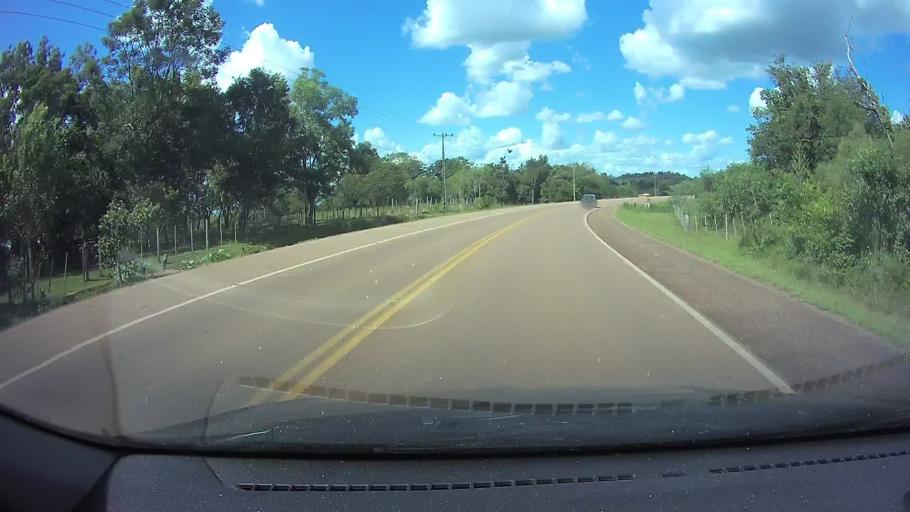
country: PY
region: Guaira
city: Itape
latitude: -25.9150
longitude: -56.7007
